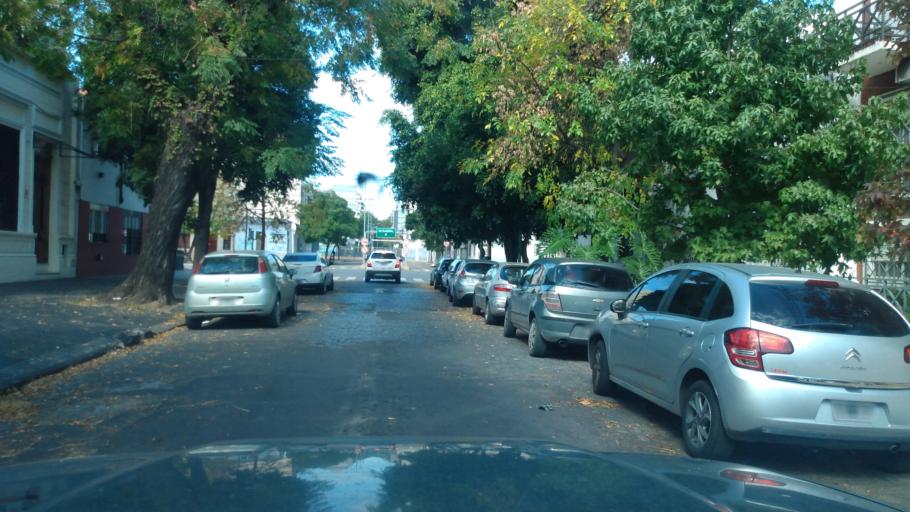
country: AR
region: Buenos Aires
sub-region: Partido de General San Martin
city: General San Martin
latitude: -34.5756
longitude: -58.4920
